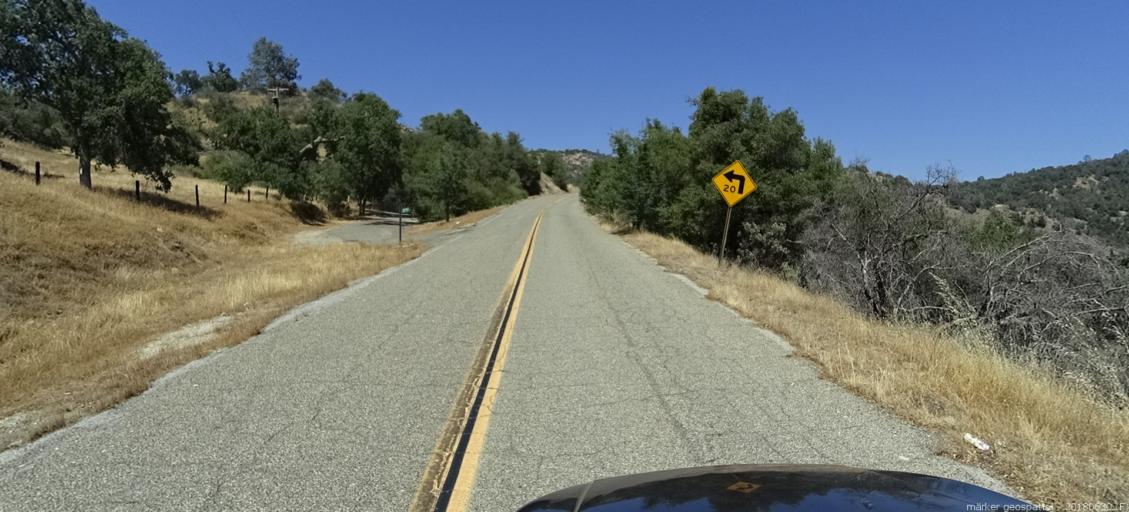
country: US
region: California
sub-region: Fresno County
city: Auberry
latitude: 37.1647
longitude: -119.5154
